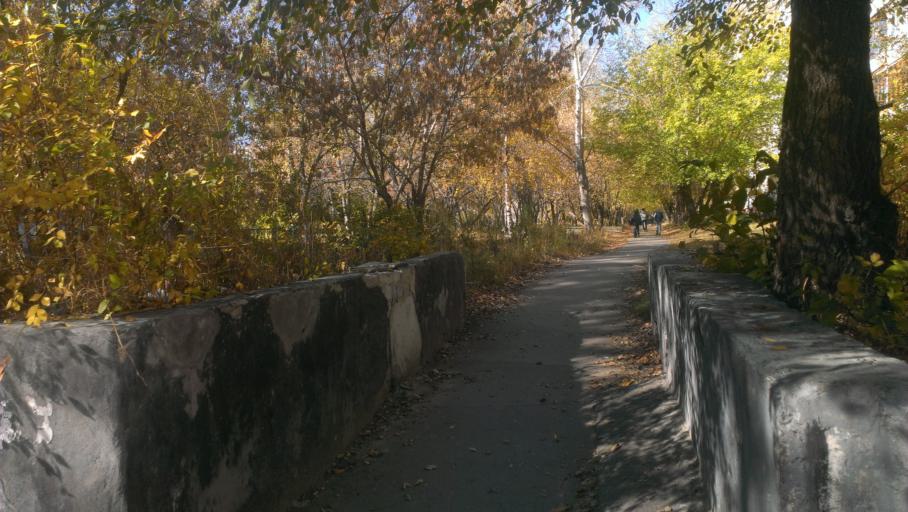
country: RU
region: Altai Krai
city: Novosilikatnyy
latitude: 53.3664
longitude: 83.6663
